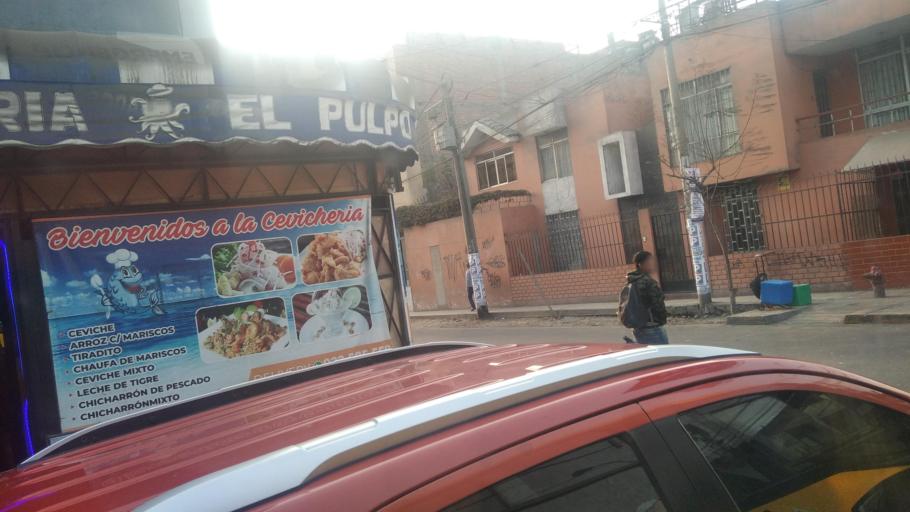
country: PE
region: Lima
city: Lima
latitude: -12.0259
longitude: -77.0003
